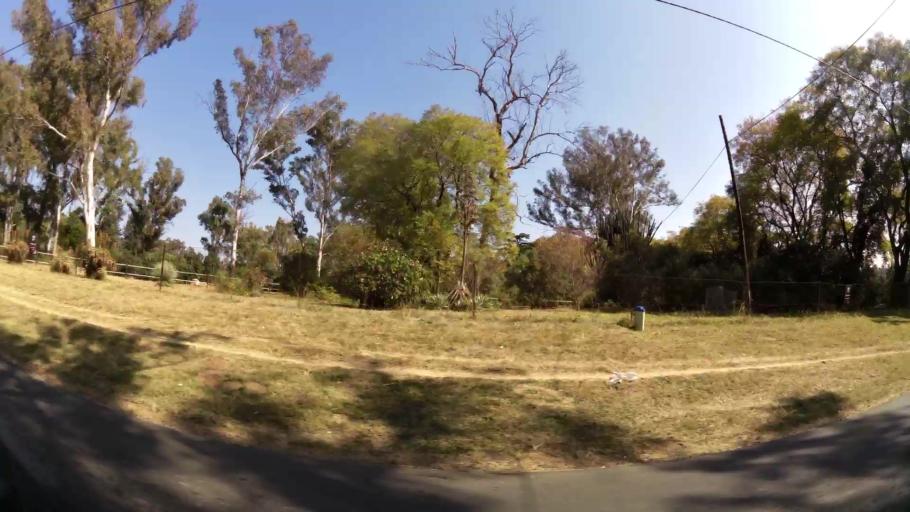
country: ZA
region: Gauteng
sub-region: City of Johannesburg Metropolitan Municipality
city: Modderfontein
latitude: -26.0959
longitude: 28.1324
